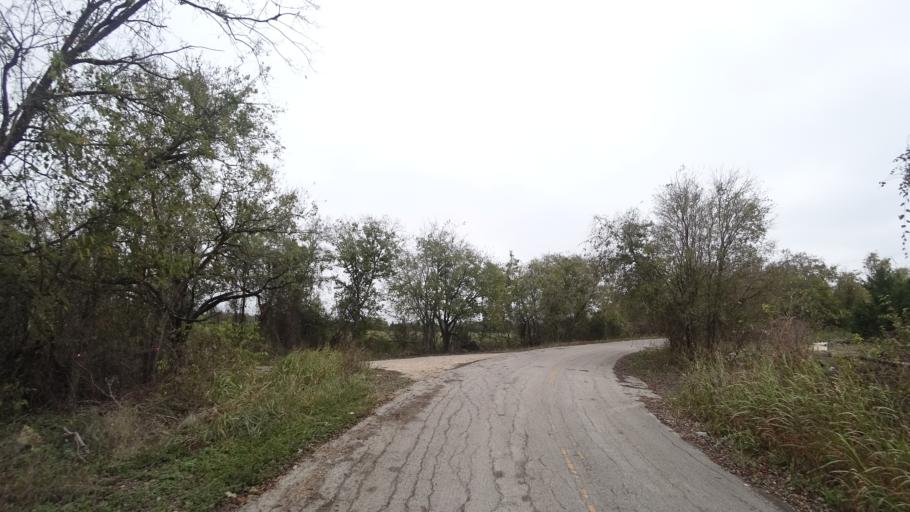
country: US
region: Texas
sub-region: Travis County
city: Pflugerville
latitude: 30.3762
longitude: -97.6276
